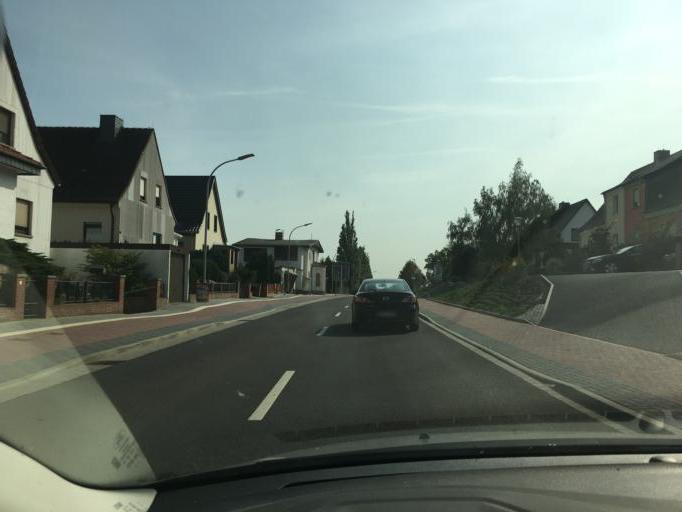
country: DE
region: Saxony-Anhalt
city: Calbe
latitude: 51.8897
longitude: 11.7695
